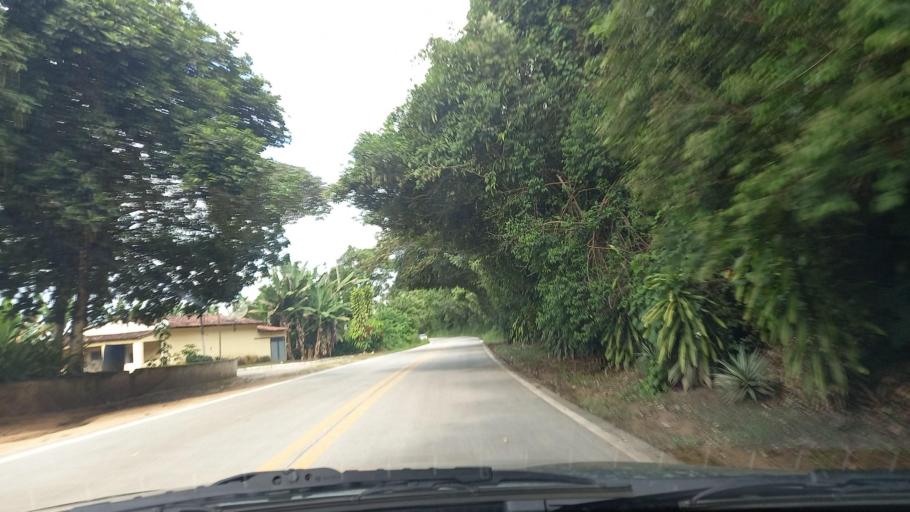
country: BR
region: Pernambuco
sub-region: Maraial
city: Maraial
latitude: -8.7906
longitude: -35.8919
